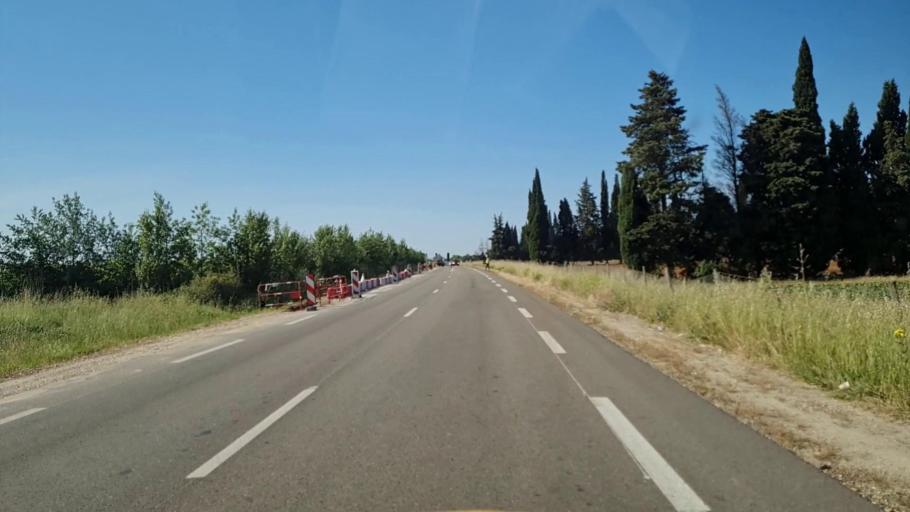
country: FR
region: Languedoc-Roussillon
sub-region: Departement du Gard
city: Garons
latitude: 43.7437
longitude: 4.4089
